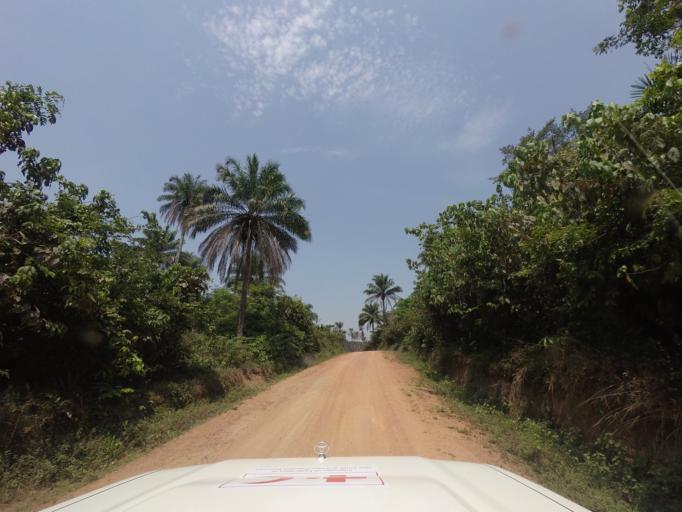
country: LR
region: Lofa
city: Voinjama
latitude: 8.4407
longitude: -9.6969
